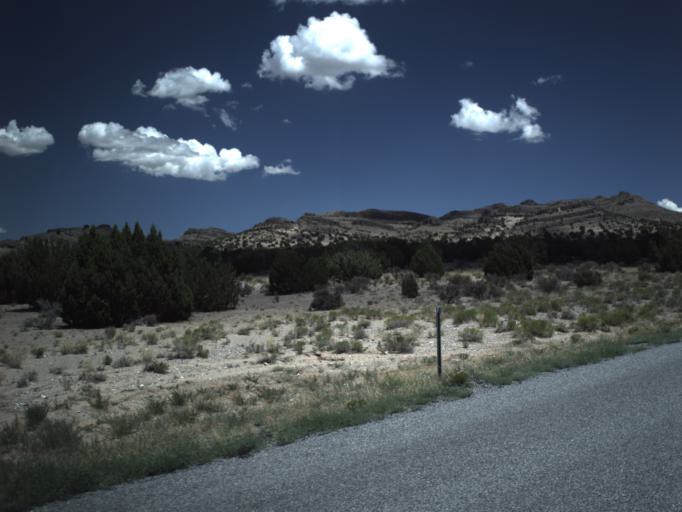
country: US
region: Utah
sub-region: Beaver County
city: Milford
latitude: 39.0708
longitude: -113.7268
